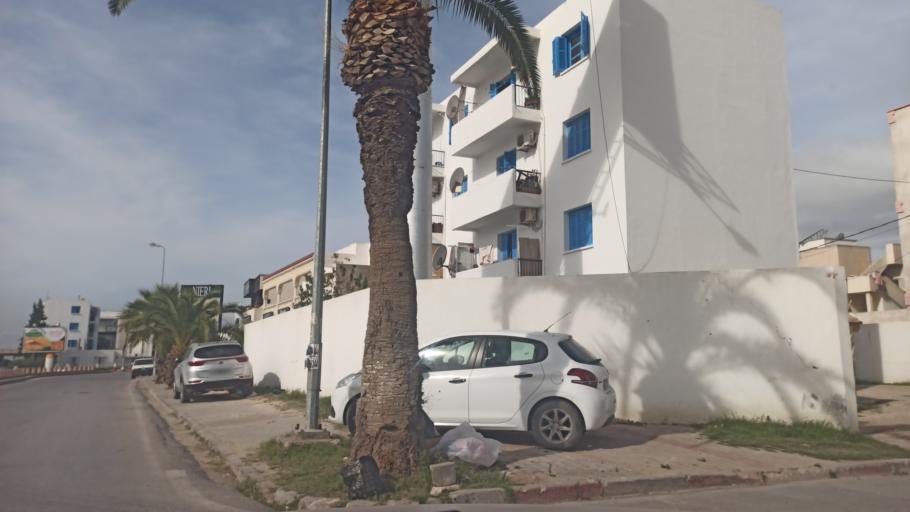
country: TN
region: Tunis
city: La Goulette
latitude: 36.8490
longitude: 10.2631
